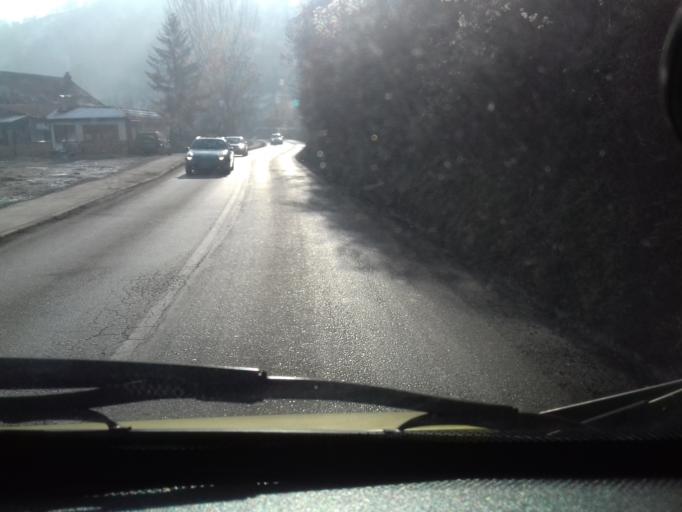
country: BA
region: Federation of Bosnia and Herzegovina
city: Zenica
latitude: 44.1888
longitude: 17.9192
